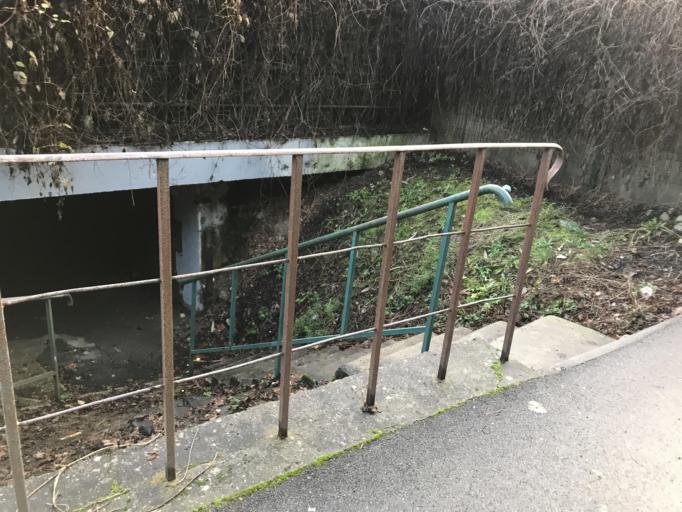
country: FR
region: Ile-de-France
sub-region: Departement de l'Essonne
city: Savigny-sur-Orge
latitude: 48.6782
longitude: 2.3546
